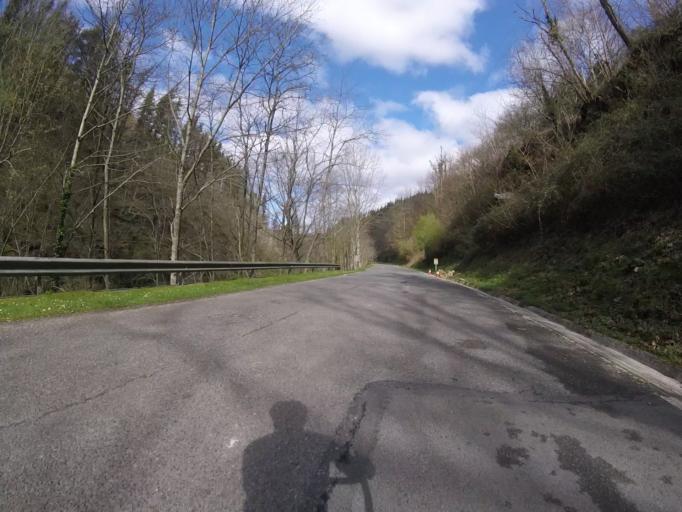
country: ES
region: Navarre
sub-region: Provincia de Navarra
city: Goizueta
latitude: 43.1613
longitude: -1.8511
